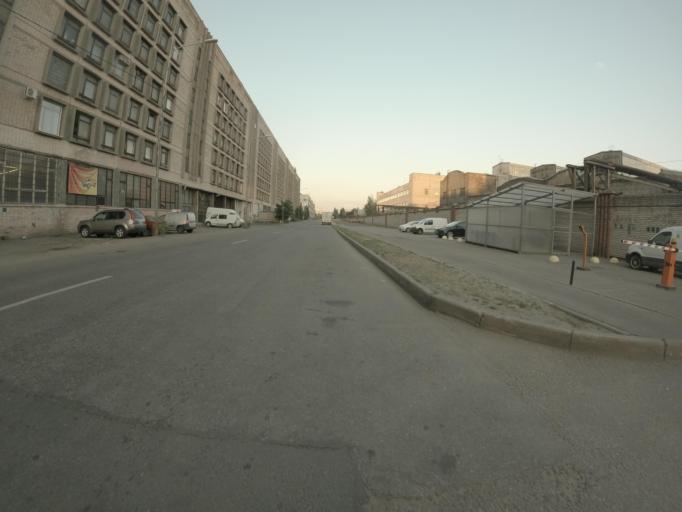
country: RU
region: St.-Petersburg
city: Admiralteisky
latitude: 59.8872
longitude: 30.2848
